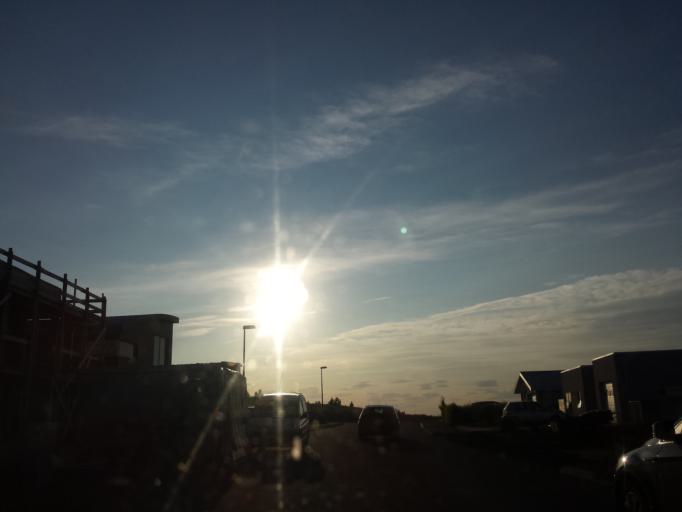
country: IS
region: Capital Region
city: Kopavogur
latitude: 64.0923
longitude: -21.8713
